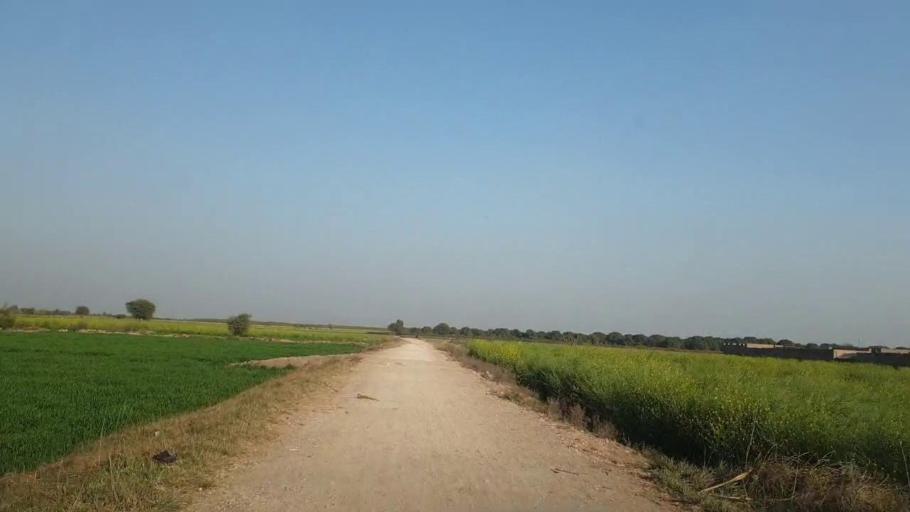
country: PK
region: Sindh
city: Tando Allahyar
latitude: 25.5820
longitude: 68.6632
